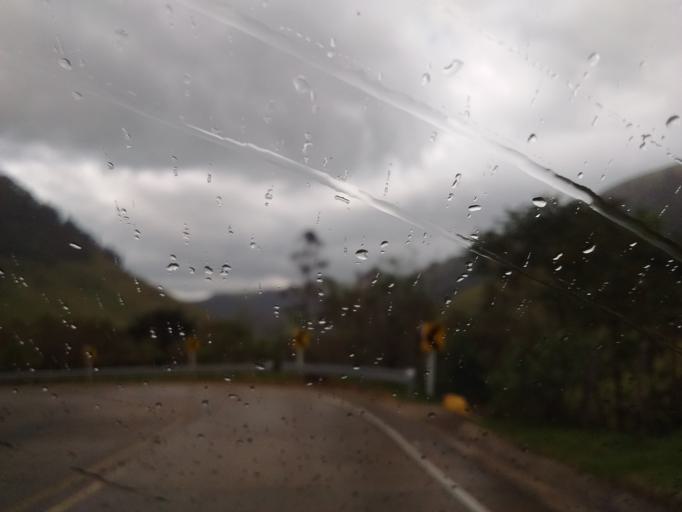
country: CO
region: Cauca
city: Paispamba
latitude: 2.3028
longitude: -76.5106
